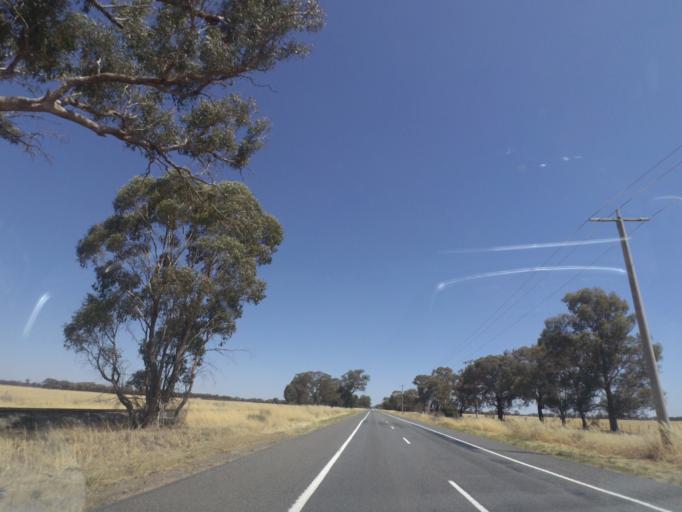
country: AU
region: Victoria
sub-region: Greater Shepparton
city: Shepparton
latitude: -36.2026
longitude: 145.4318
